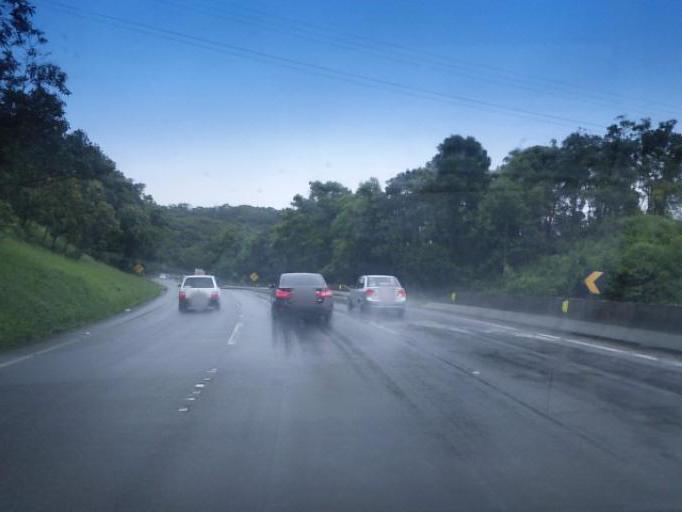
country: BR
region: Parana
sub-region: Sao Jose Dos Pinhais
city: Sao Jose dos Pinhais
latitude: -25.8460
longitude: -49.0031
